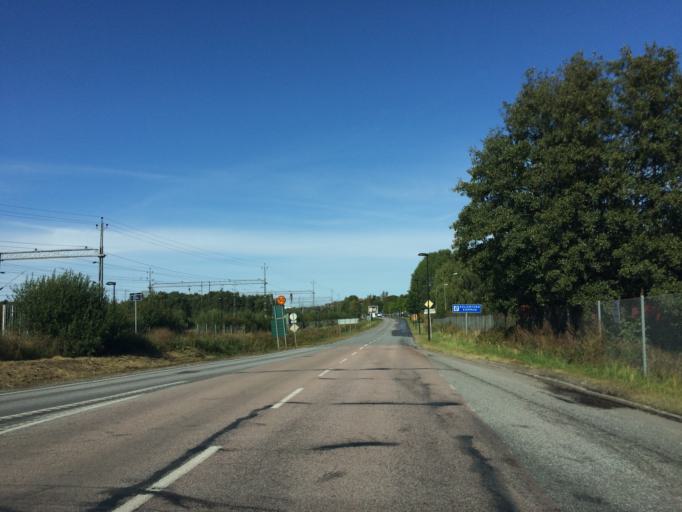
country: SE
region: Stockholm
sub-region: Solna Kommun
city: Rasunda
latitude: 59.3957
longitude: 17.9865
